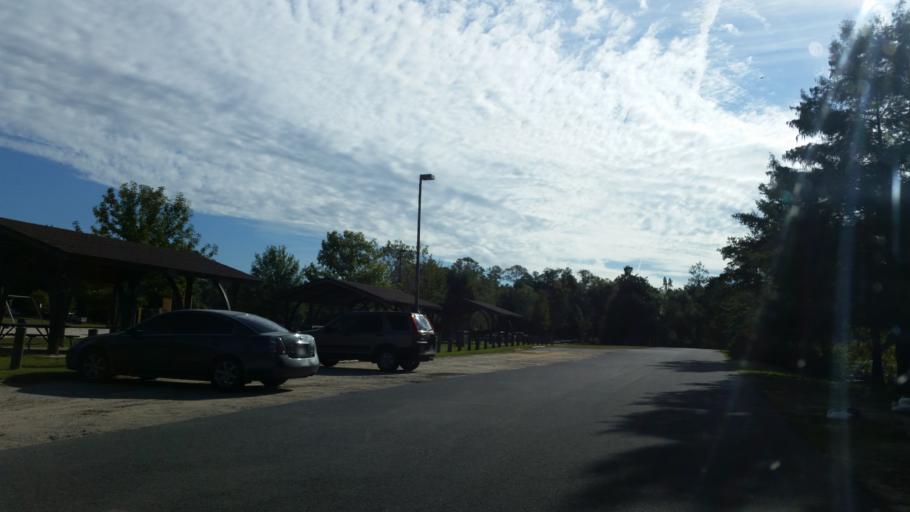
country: US
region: Florida
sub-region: Santa Rosa County
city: Milton
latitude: 30.6328
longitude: -87.0371
